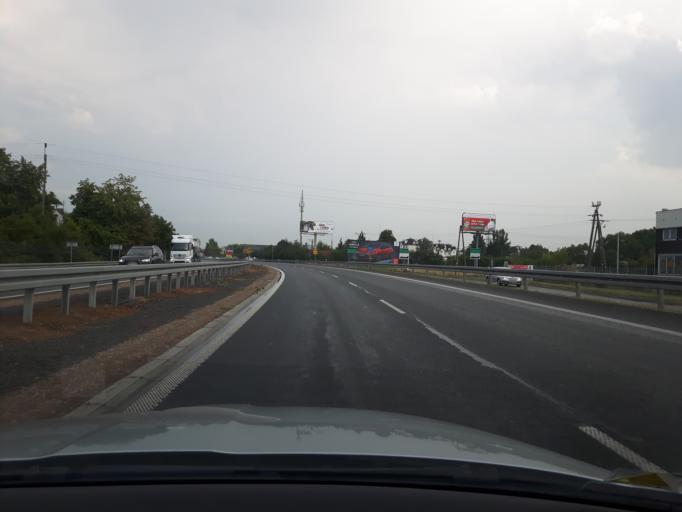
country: PL
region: Masovian Voivodeship
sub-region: Powiat warszawski zachodni
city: Kielpin
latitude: 52.3413
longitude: 20.8669
